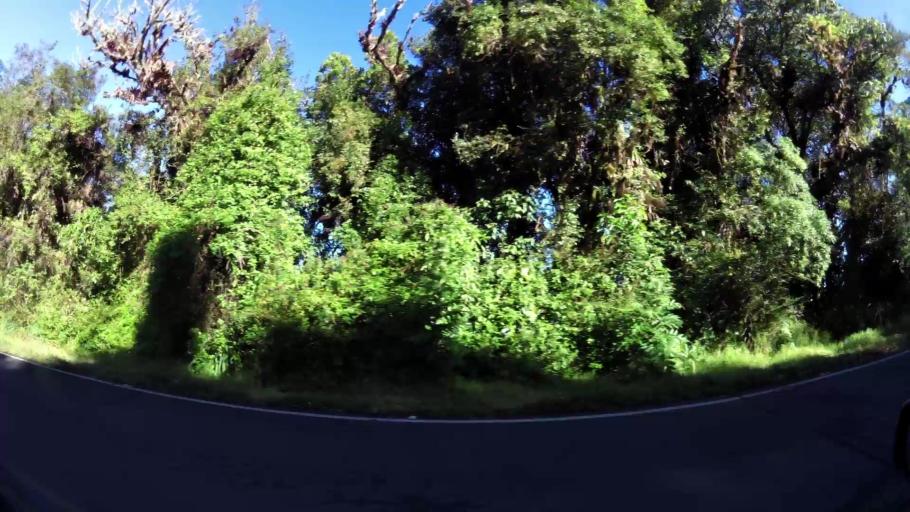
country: CR
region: San Jose
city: San Marcos
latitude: 9.7011
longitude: -83.9383
